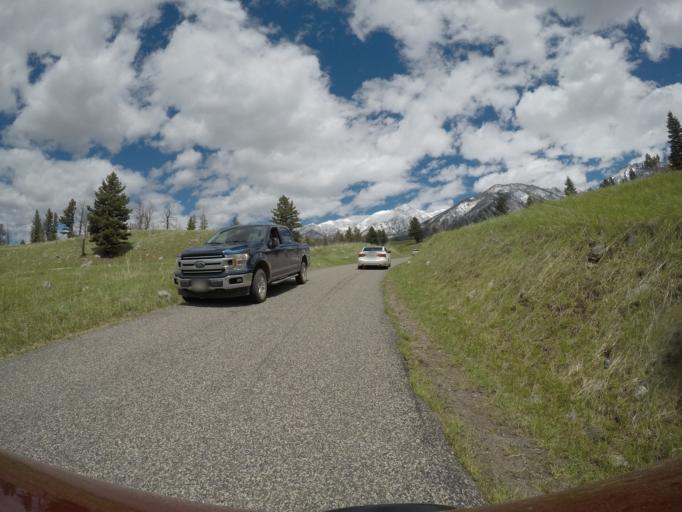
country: US
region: Montana
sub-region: Park County
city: Livingston
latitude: 45.4994
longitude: -110.5516
